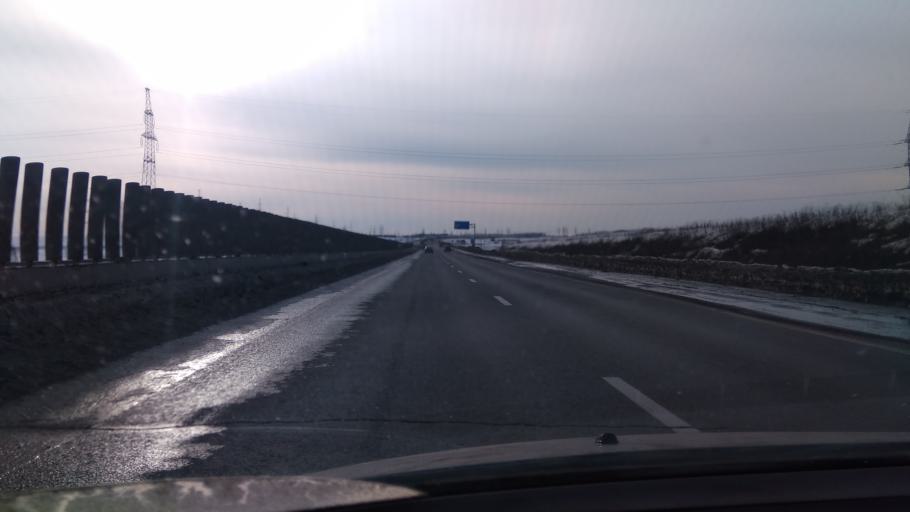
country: RU
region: Perm
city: Ferma
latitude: 57.9318
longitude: 56.3404
